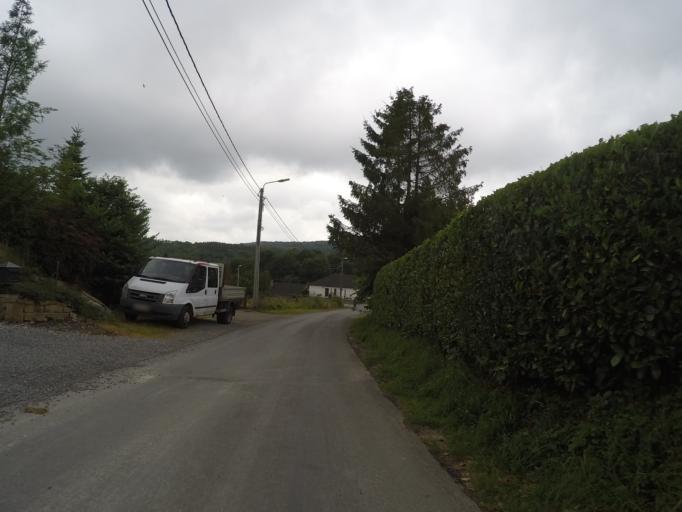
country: BE
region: Wallonia
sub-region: Province de Namur
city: Yvoir
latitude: 50.3332
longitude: 4.9048
